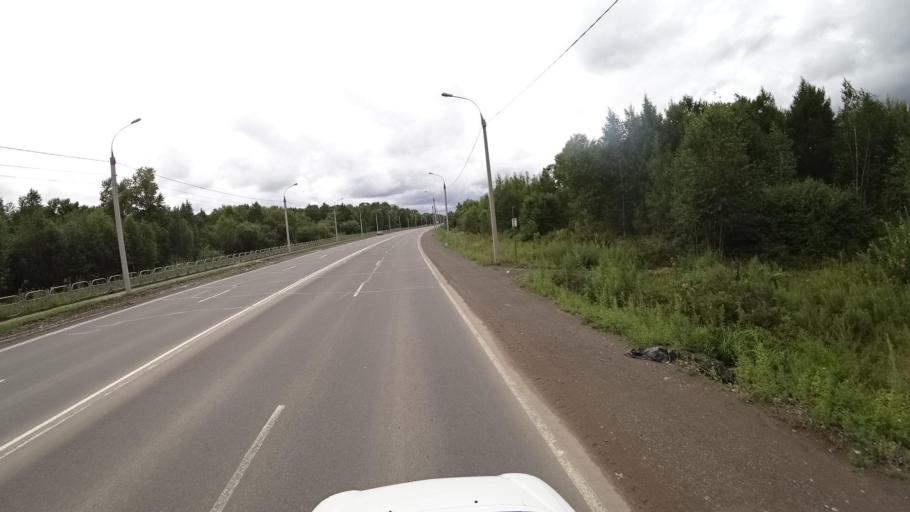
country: RU
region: Khabarovsk Krai
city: Solnechnyy
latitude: 50.5872
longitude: 137.0272
